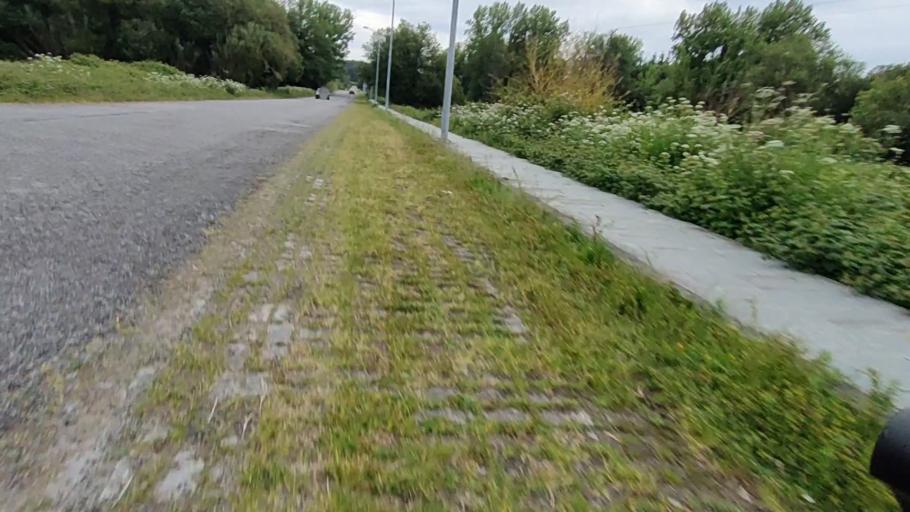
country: ES
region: Galicia
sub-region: Provincia da Coruna
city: Boiro
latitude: 42.6131
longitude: -8.8690
